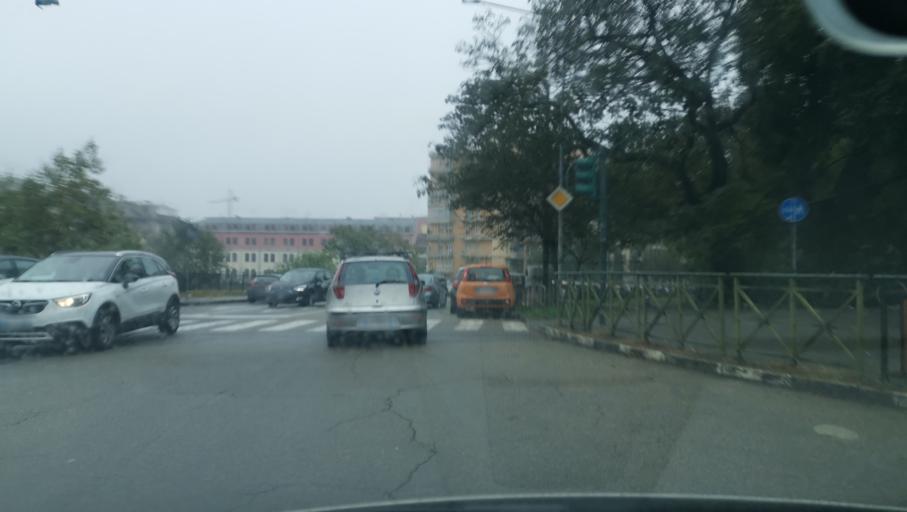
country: IT
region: Piedmont
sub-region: Provincia di Torino
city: Turin
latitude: 45.0816
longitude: 7.6869
